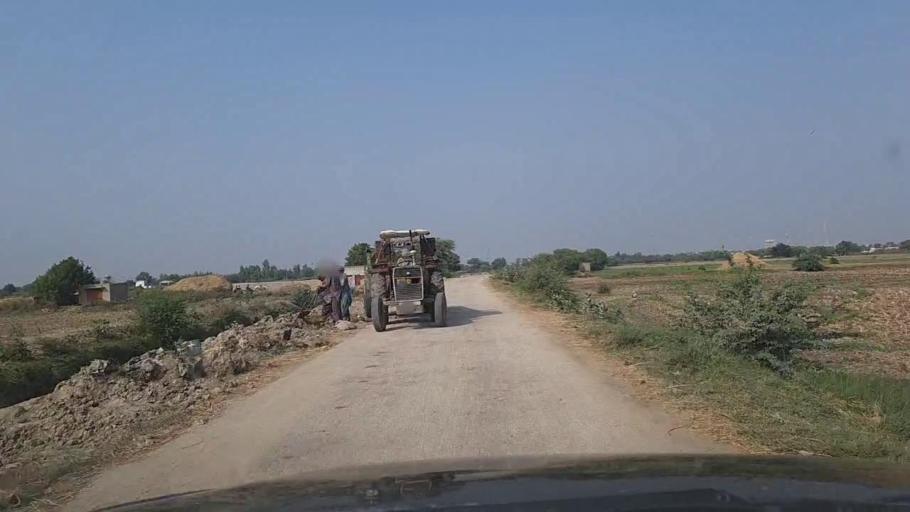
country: PK
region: Sindh
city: Mirpur Batoro
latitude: 24.7168
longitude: 68.2550
